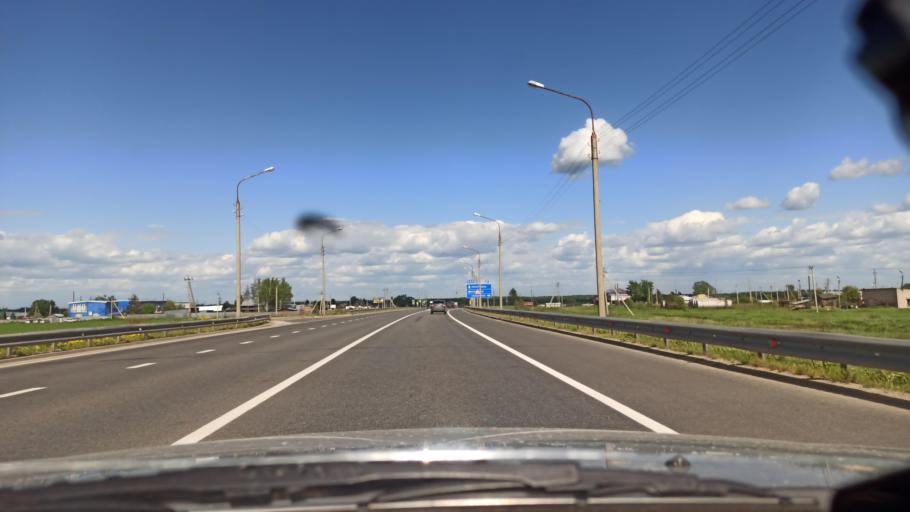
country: RU
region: Vologda
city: Vologda
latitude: 59.2863
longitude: 39.8501
